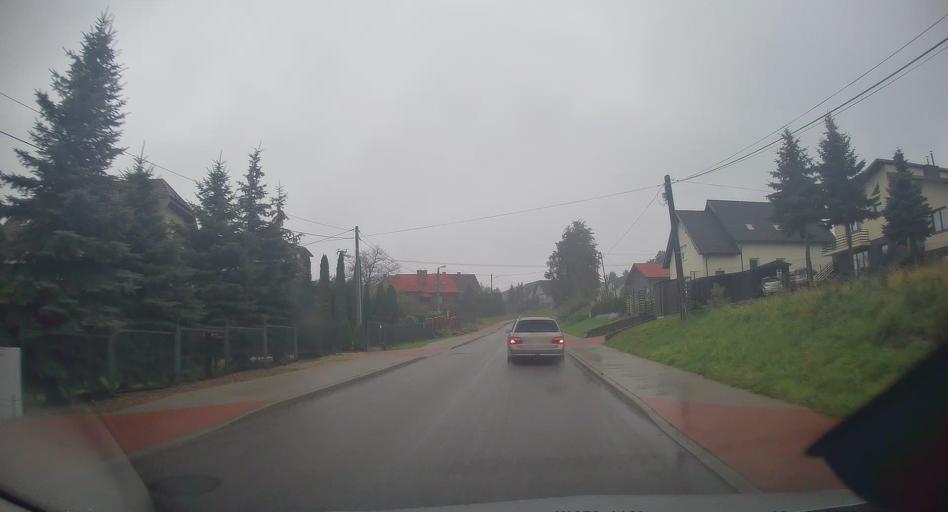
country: PL
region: Lesser Poland Voivodeship
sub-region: Powiat krakowski
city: Ochojno
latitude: 49.9540
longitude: 19.9763
